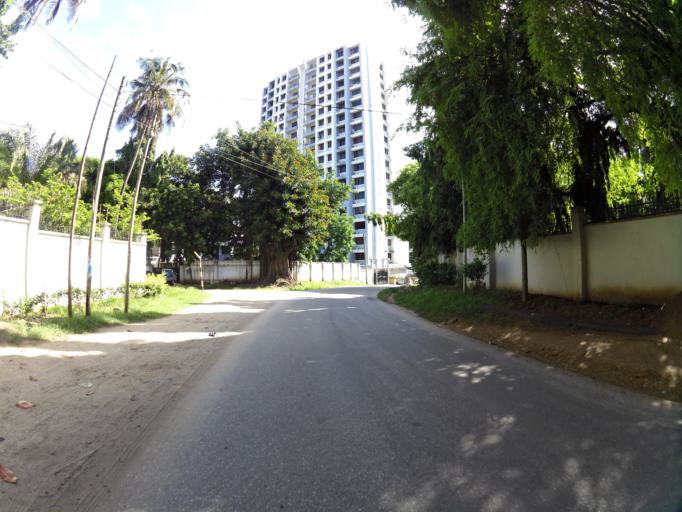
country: TZ
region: Dar es Salaam
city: Dar es Salaam
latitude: -6.7997
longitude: 39.2750
